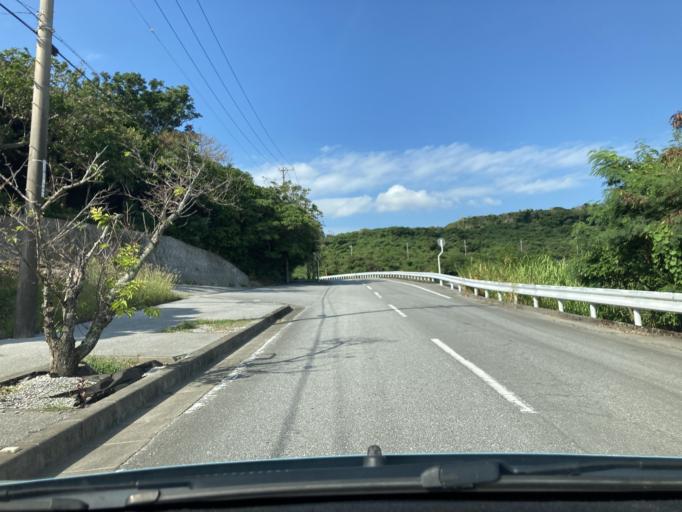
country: JP
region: Okinawa
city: Ginowan
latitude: 26.2798
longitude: 127.7991
